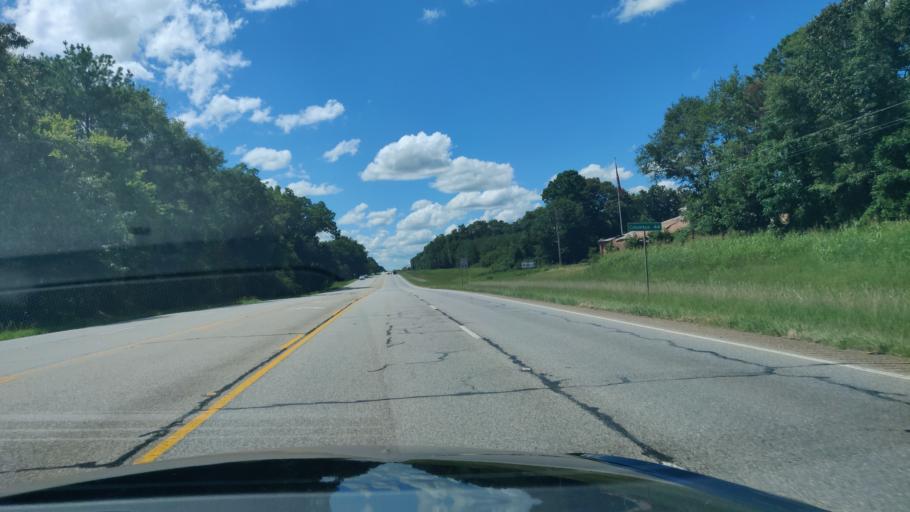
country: US
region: Georgia
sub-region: Webster County
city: Preston
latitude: 31.9770
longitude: -84.6162
